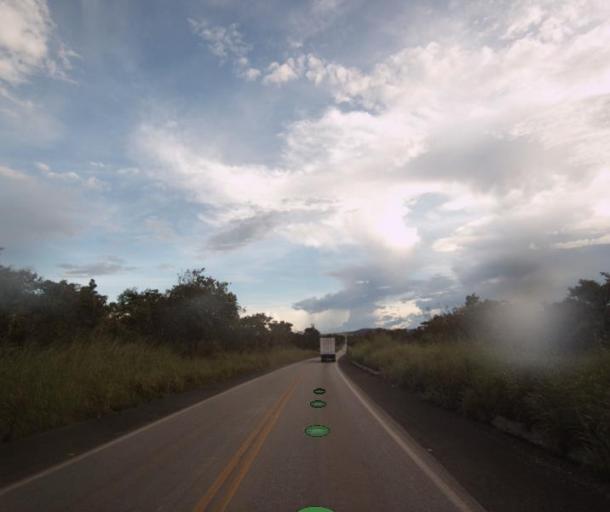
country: BR
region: Goias
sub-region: Uruacu
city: Uruacu
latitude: -14.0583
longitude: -49.0911
